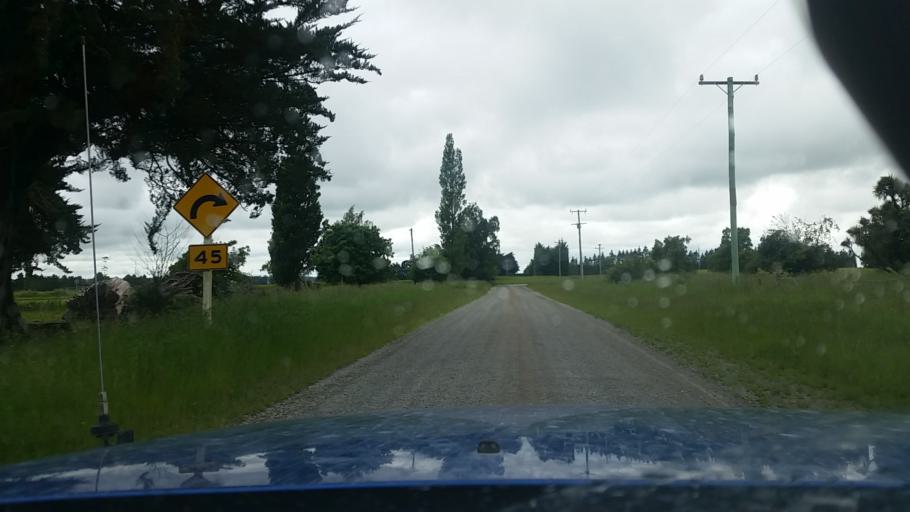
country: NZ
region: Canterbury
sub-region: Ashburton District
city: Methven
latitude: -43.6959
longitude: 171.4298
